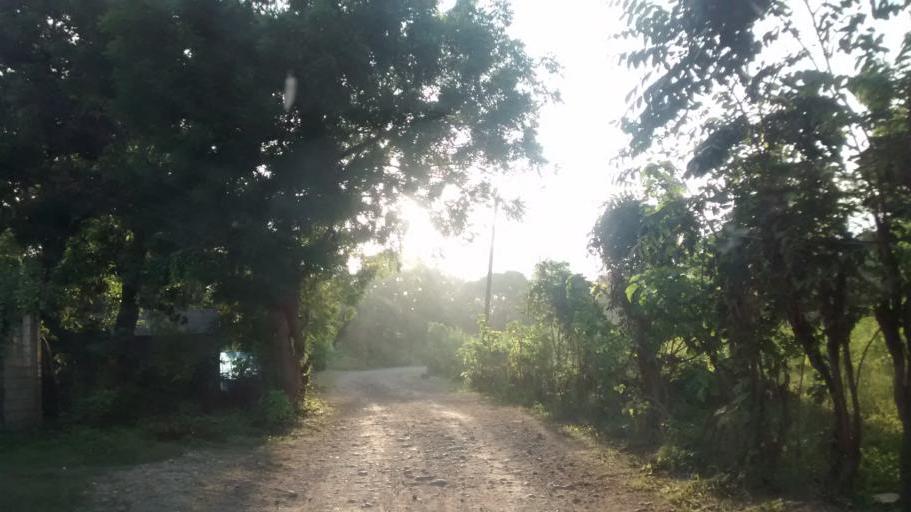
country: HT
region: Ouest
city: Grangwav
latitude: 18.4263
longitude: -72.7839
